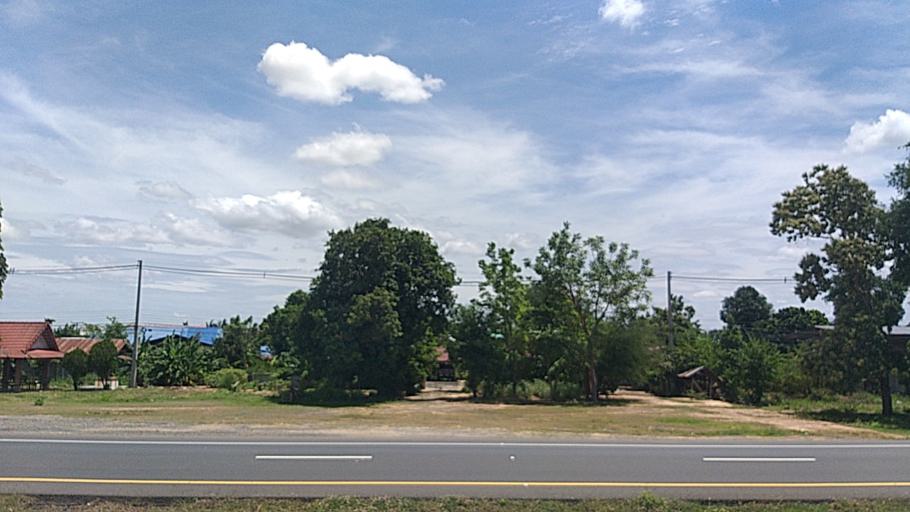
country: TH
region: Buriram
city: Prakhon Chai
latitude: 14.6268
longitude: 103.2542
